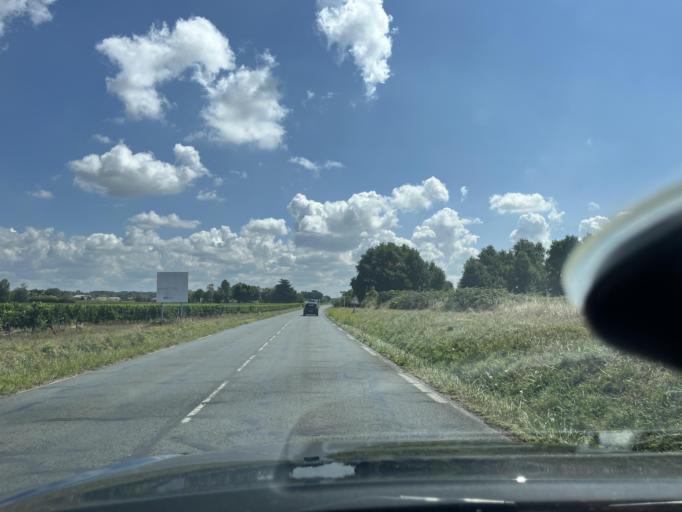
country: FR
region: Aquitaine
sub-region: Departement de la Gironde
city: Berson
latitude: 45.0619
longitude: -0.6119
